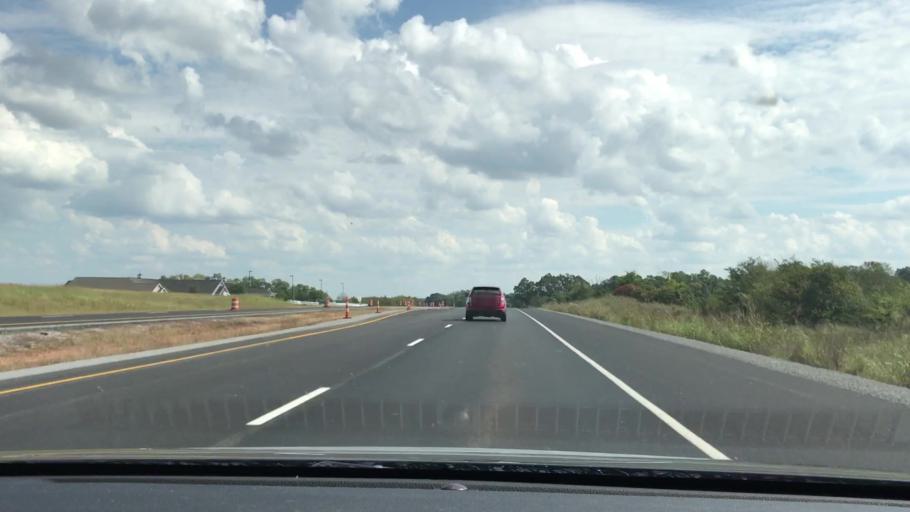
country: US
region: Kentucky
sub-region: Trigg County
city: Cadiz
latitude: 36.8602
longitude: -87.8068
